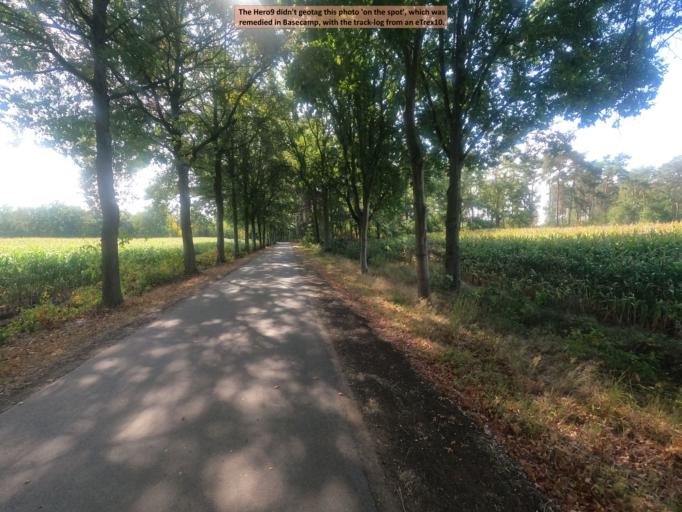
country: BE
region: Flanders
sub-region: Provincie Antwerpen
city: Lille
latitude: 51.2719
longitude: 4.8461
